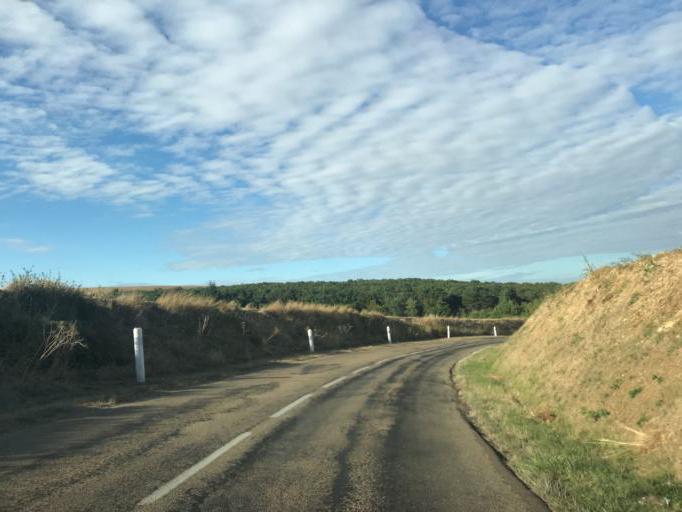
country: FR
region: Bourgogne
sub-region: Departement de l'Yonne
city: Fontenailles
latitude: 47.5952
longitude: 3.4735
